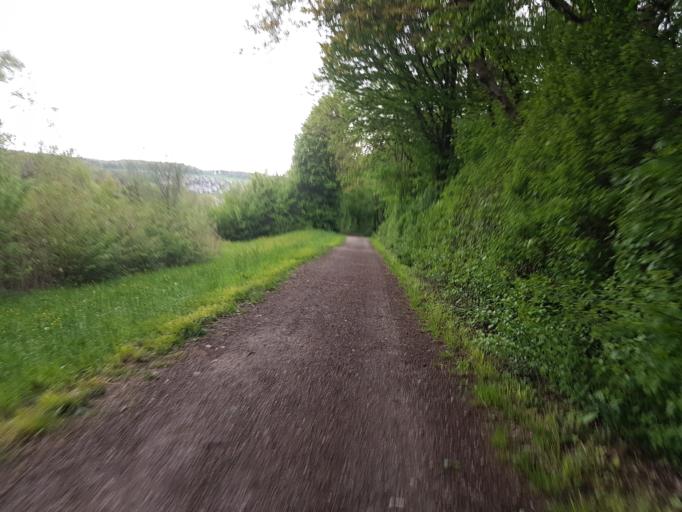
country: DE
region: Baden-Wuerttemberg
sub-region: Freiburg Region
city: Lauchringen
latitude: 47.6267
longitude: 8.2997
